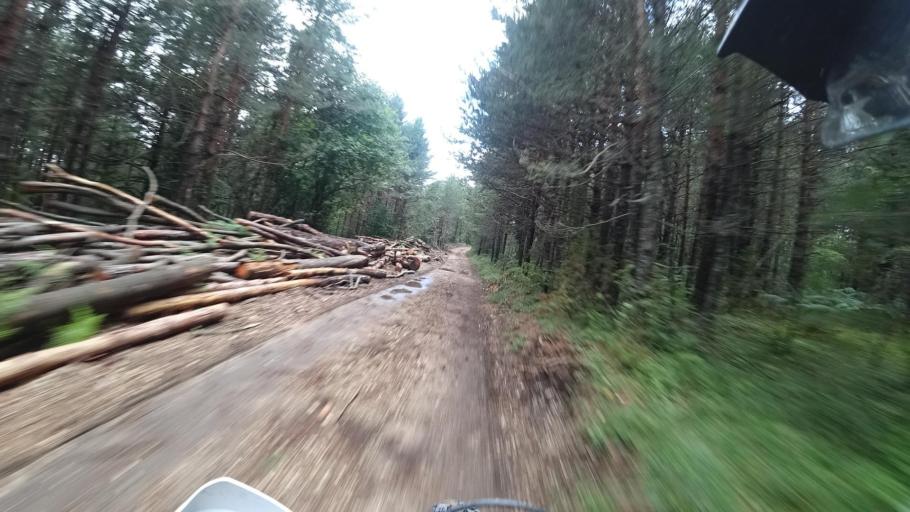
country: HR
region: Licko-Senjska
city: Otocac
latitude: 44.8698
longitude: 15.4038
